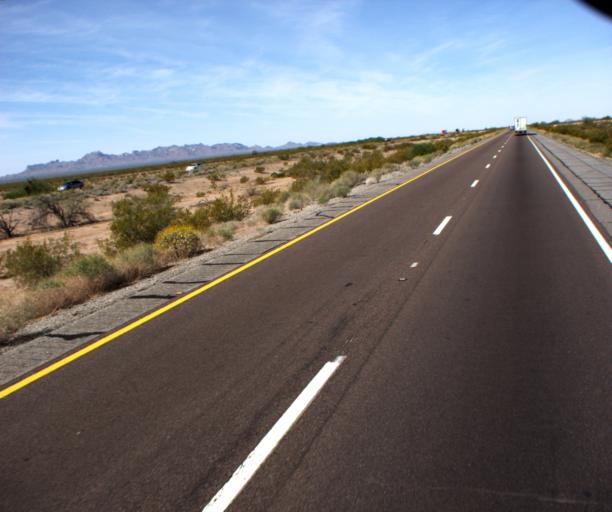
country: US
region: Arizona
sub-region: La Paz County
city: Salome
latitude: 33.5511
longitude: -113.2334
